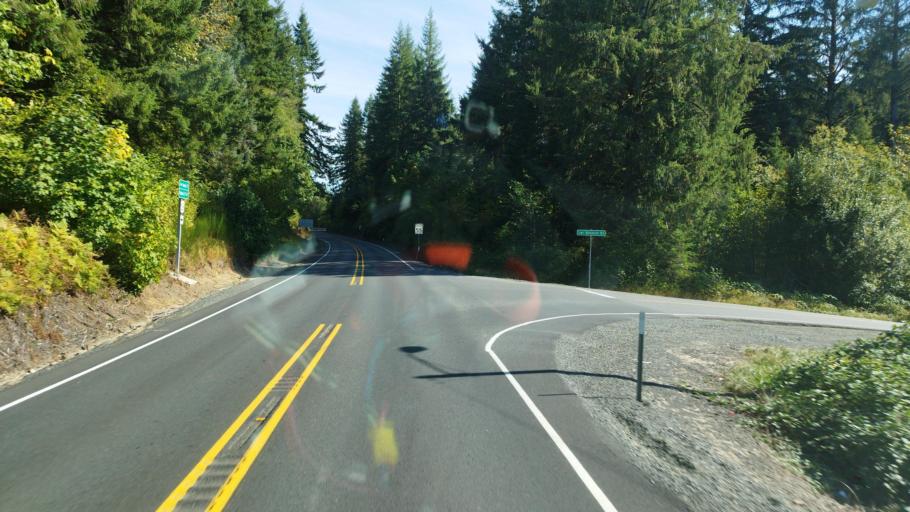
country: US
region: Oregon
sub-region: Clatsop County
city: Seaside
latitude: 45.8645
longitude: -123.5911
